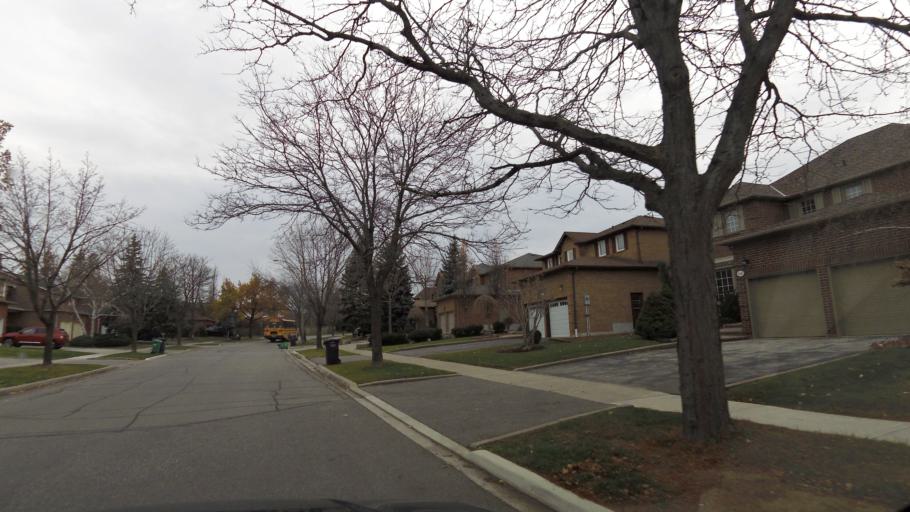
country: CA
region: Ontario
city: Etobicoke
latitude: 43.6343
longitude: -79.6053
